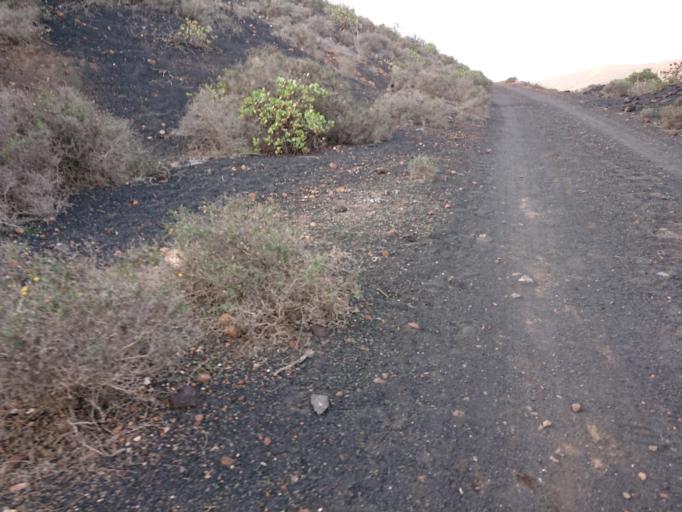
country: ES
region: Canary Islands
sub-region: Provincia de Las Palmas
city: Tinajo
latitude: 29.0160
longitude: -13.6931
